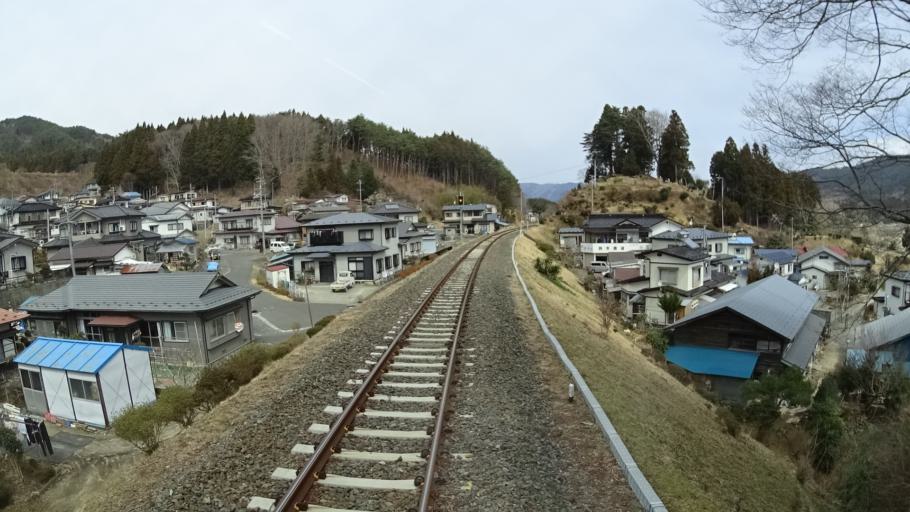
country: JP
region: Iwate
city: Yamada
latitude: 39.4251
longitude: 141.9718
